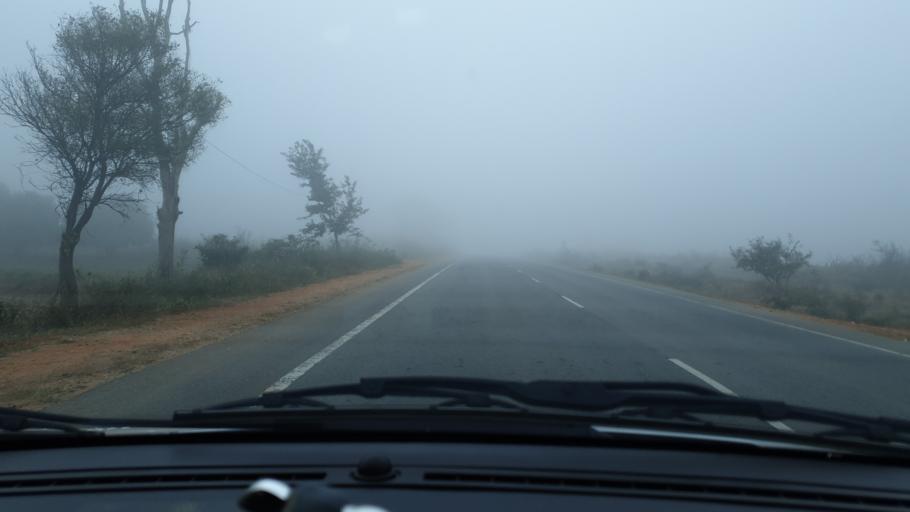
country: IN
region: Telangana
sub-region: Mahbubnagar
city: Nagar Karnul
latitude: 16.6848
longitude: 78.5241
